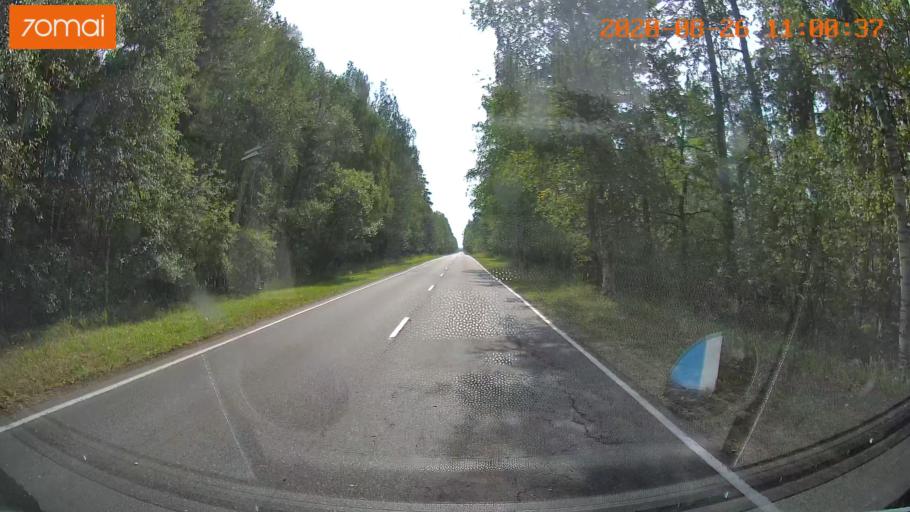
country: RU
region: Rjazan
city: Izhevskoye
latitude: 54.5731
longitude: 41.2148
